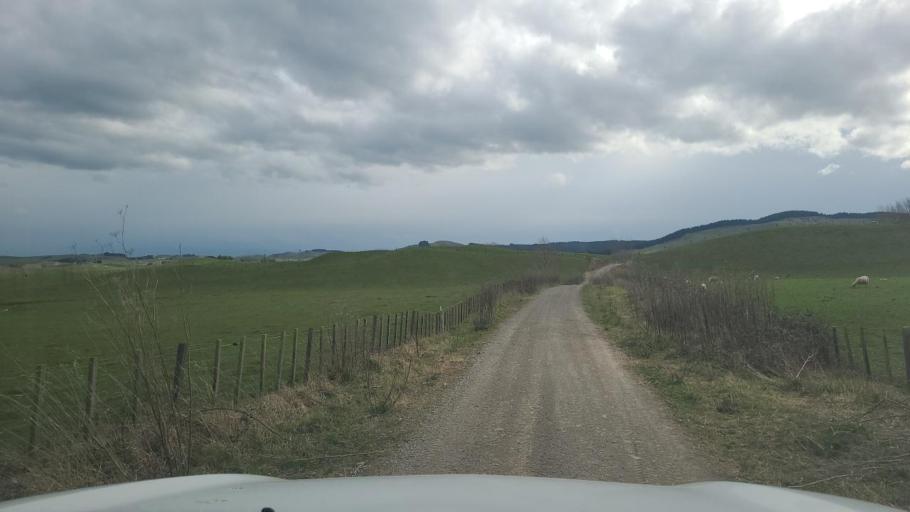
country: NZ
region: Hawke's Bay
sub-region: Napier City
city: Taradale
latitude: -39.5225
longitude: 176.7047
